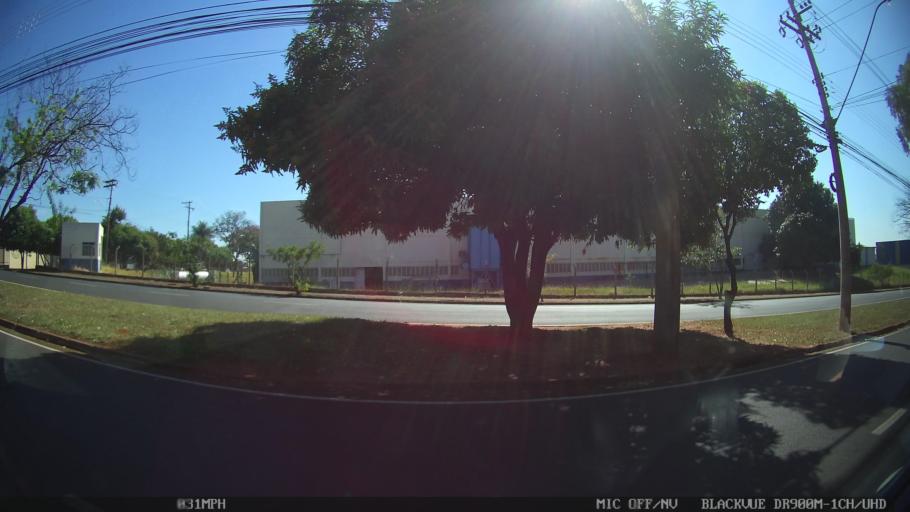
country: BR
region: Sao Paulo
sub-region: Sao Jose Do Rio Preto
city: Sao Jose do Rio Preto
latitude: -20.8110
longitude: -49.4181
